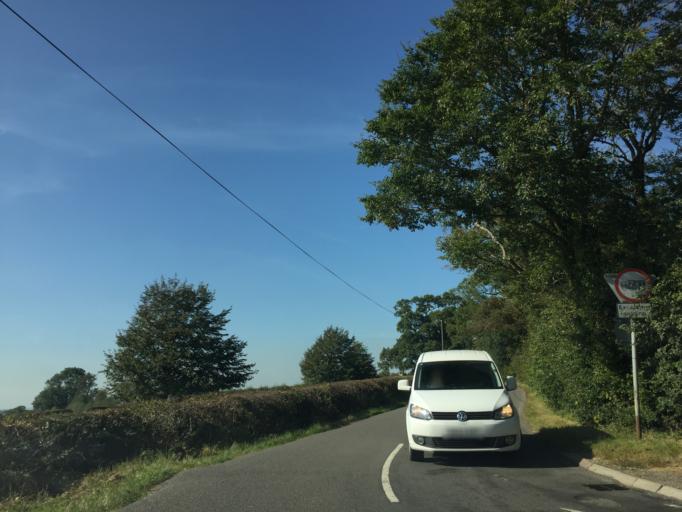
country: GB
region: England
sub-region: Leicestershire
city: Houghton on the Hill
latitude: 52.6748
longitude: -0.9371
